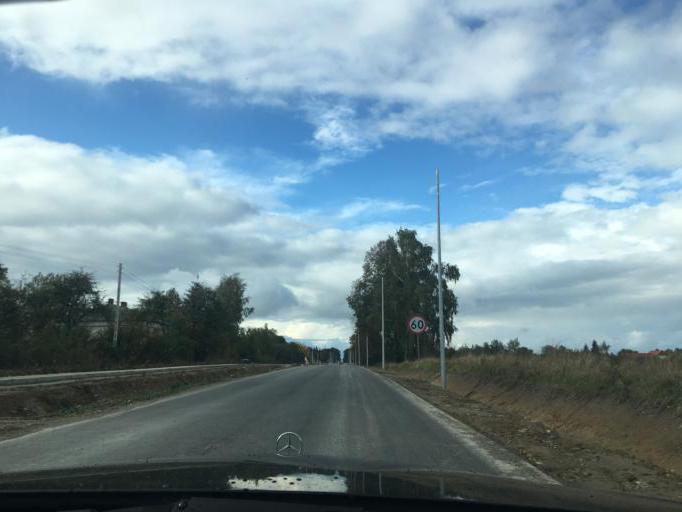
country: PL
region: Lublin Voivodeship
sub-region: Powiat lubelski
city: Krzczonow
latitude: 51.0069
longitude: 22.6703
